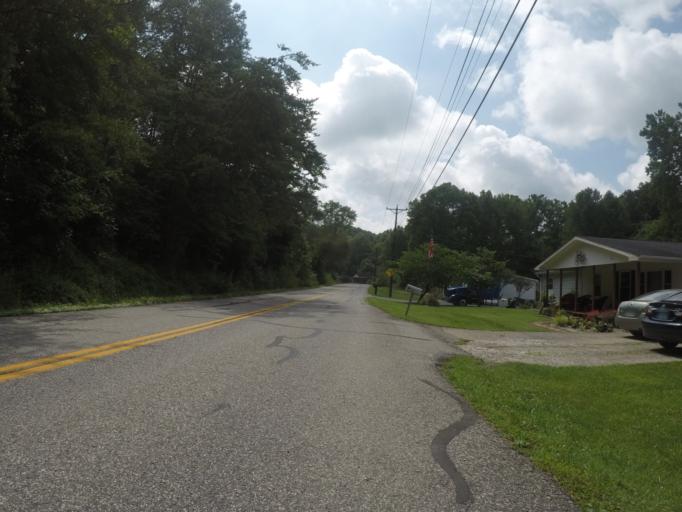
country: US
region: Kentucky
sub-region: Boyd County
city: Meads
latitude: 38.4157
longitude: -82.6892
